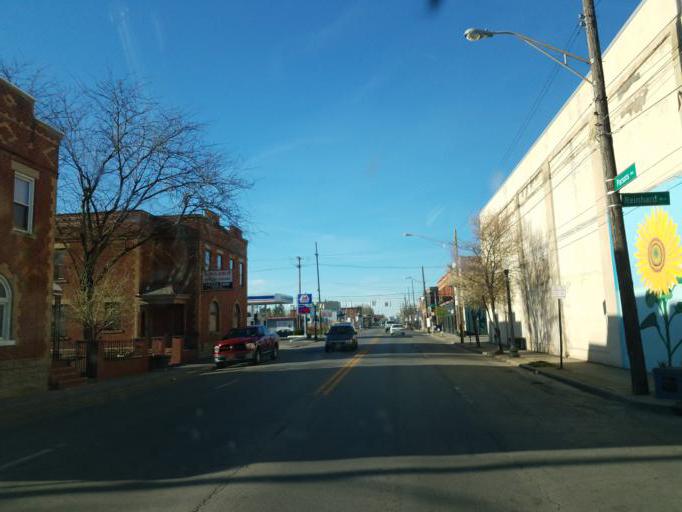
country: US
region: Ohio
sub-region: Franklin County
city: Columbus
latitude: 39.9432
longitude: -82.9831
